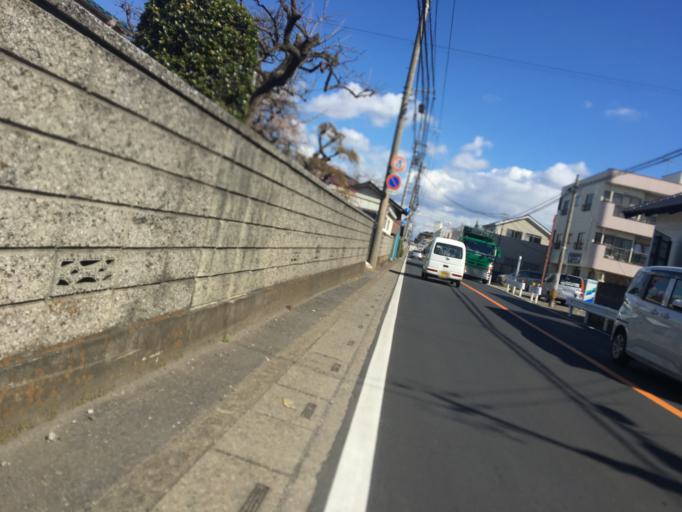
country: JP
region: Saitama
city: Shiki
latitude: 35.8111
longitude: 139.5511
